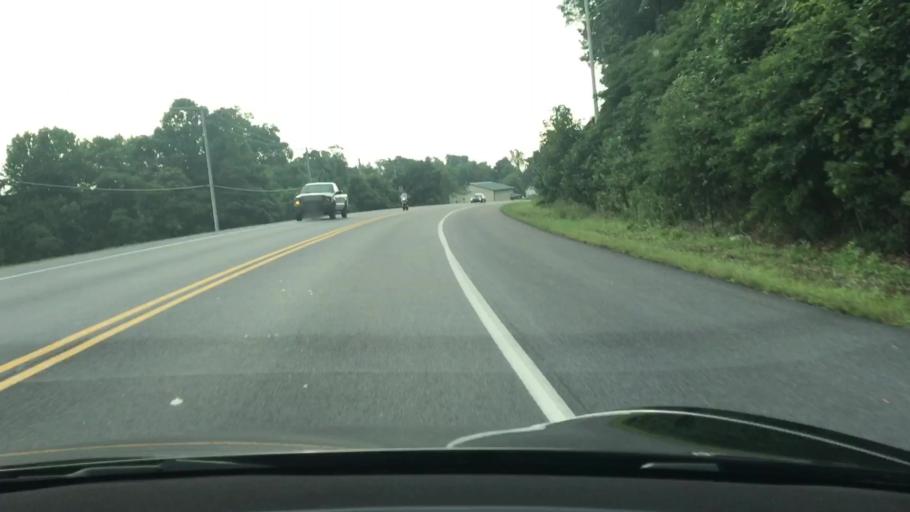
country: US
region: Pennsylvania
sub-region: York County
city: Valley Green
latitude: 40.1337
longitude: -76.8061
